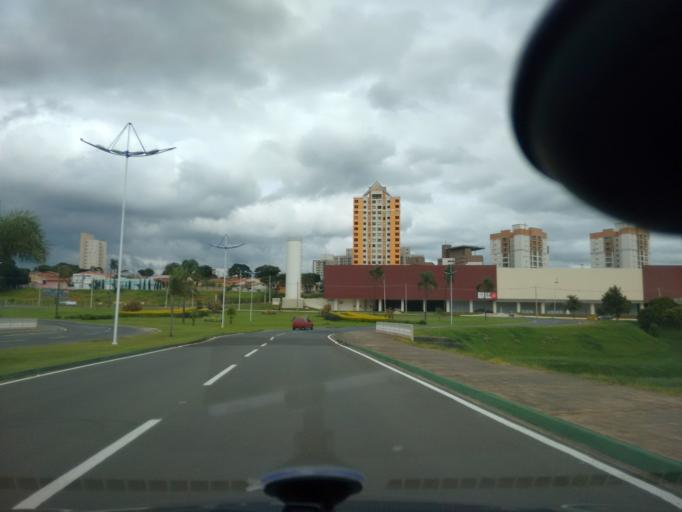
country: BR
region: Sao Paulo
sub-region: Indaiatuba
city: Indaiatuba
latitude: -23.0936
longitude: -47.2266
